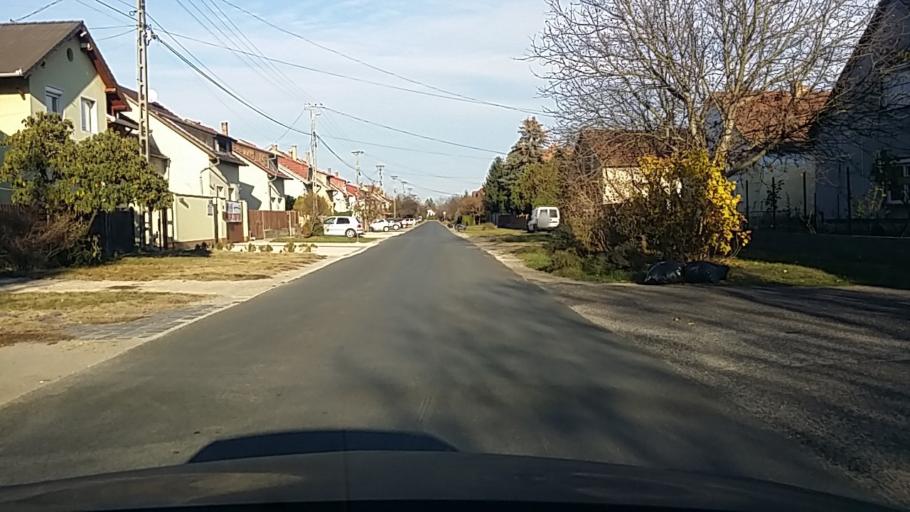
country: HU
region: Pest
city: Szigetszentmiklos
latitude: 47.3505
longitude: 19.0187
